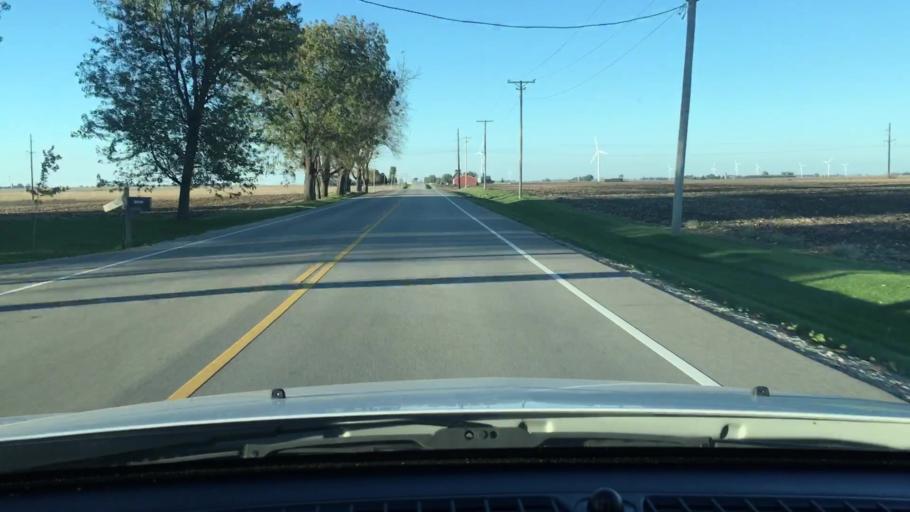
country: US
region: Illinois
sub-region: DeKalb County
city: Malta
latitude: 41.8236
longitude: -88.8864
